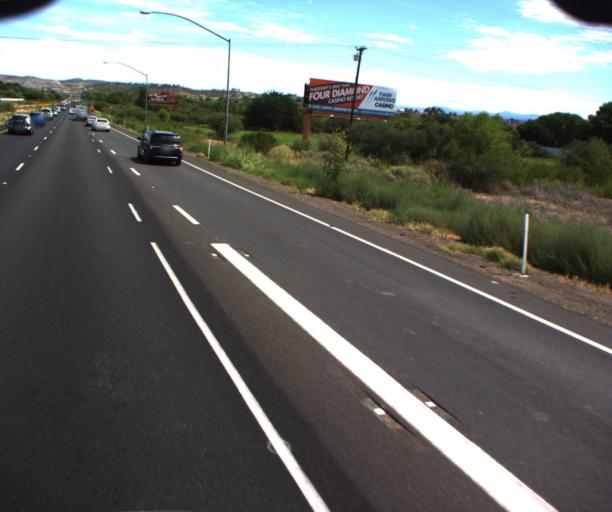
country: US
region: Arizona
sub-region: Yavapai County
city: Camp Verde
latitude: 34.5827
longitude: -111.8814
